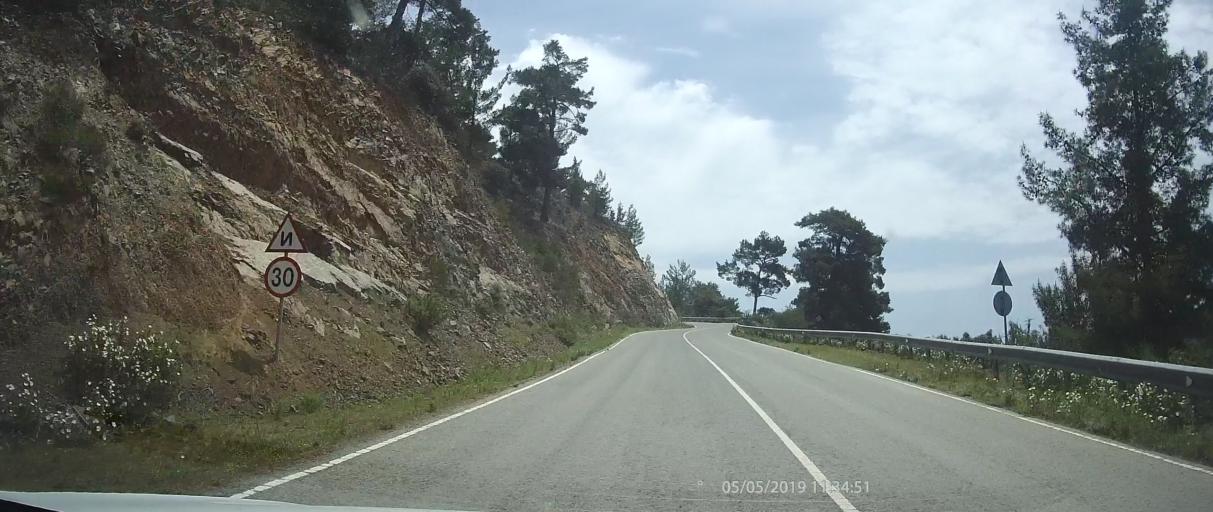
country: CY
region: Lefkosia
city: Kato Pyrgos
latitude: 34.9661
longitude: 32.6499
